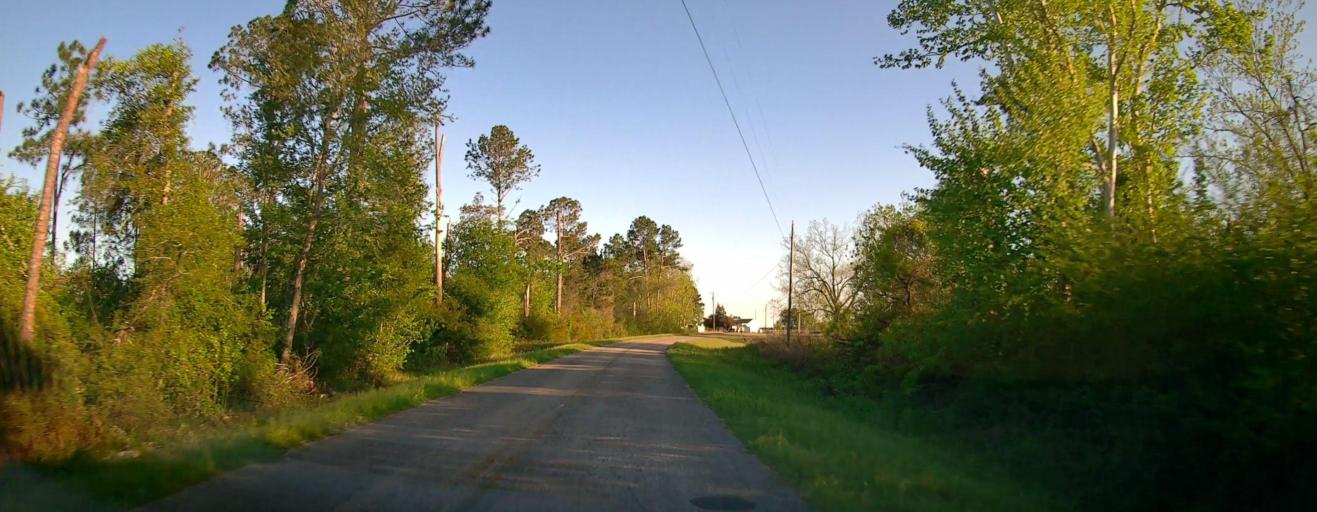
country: US
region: Georgia
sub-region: Ben Hill County
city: Fitzgerald
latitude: 31.6657
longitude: -83.2103
